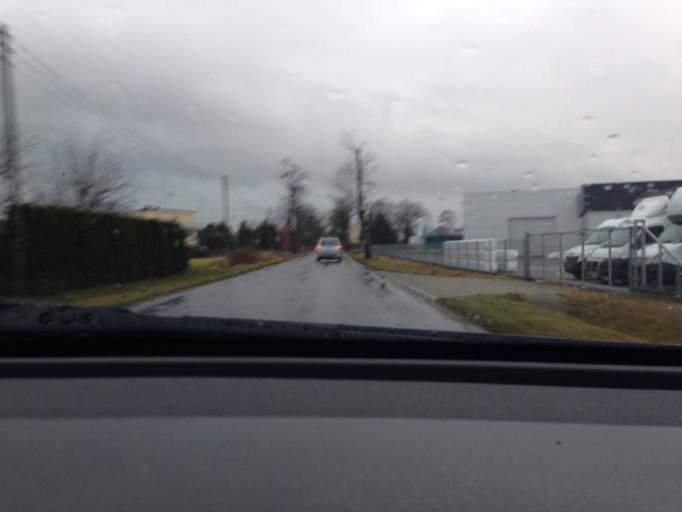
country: PL
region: Opole Voivodeship
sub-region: Powiat opolski
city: Wegry
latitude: 50.7296
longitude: 18.0407
